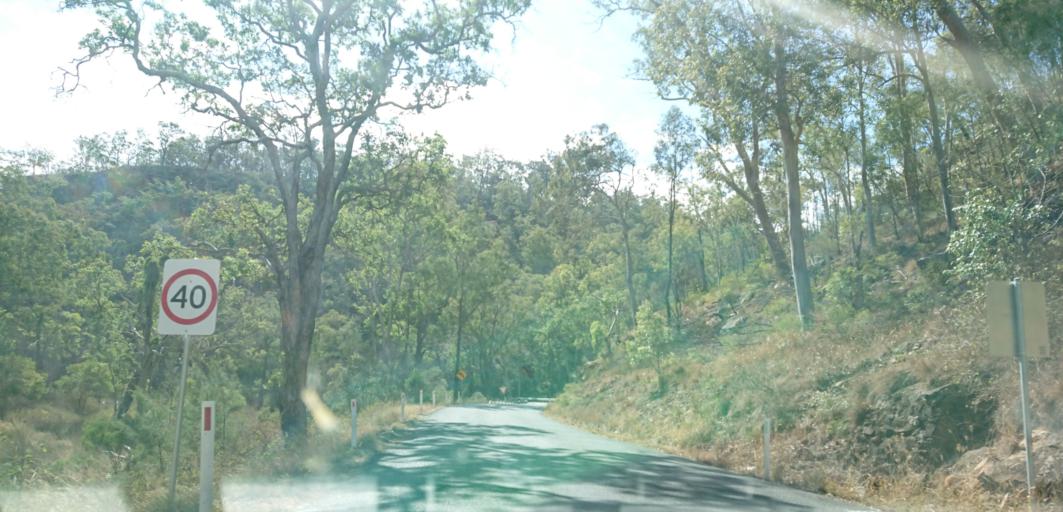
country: AU
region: Queensland
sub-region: Toowoomba
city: Top Camp
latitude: -27.7687
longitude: 152.0889
